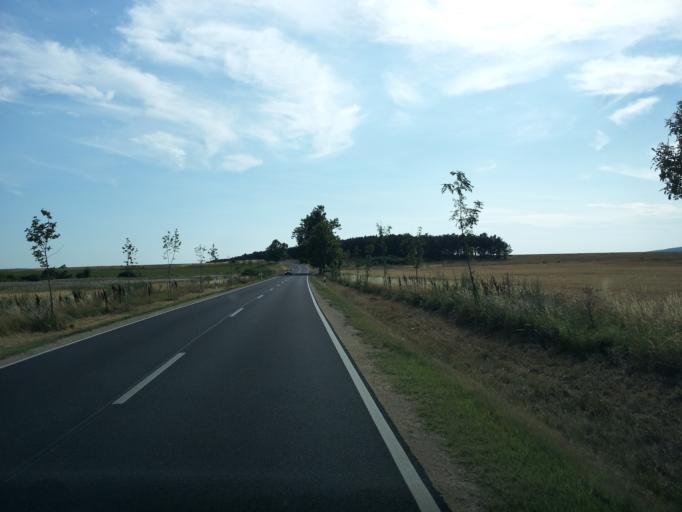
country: HU
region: Veszprem
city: Nemesvamos
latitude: 47.0147
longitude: 17.7661
